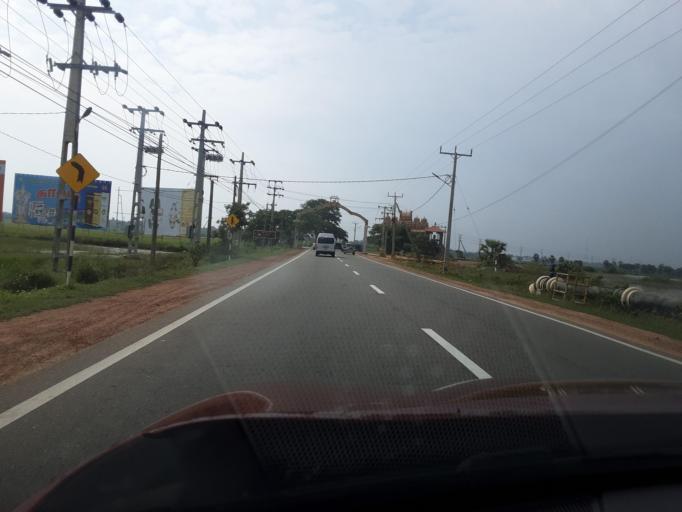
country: LK
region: Northern Province
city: Jaffna
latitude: 9.6629
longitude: 80.0637
